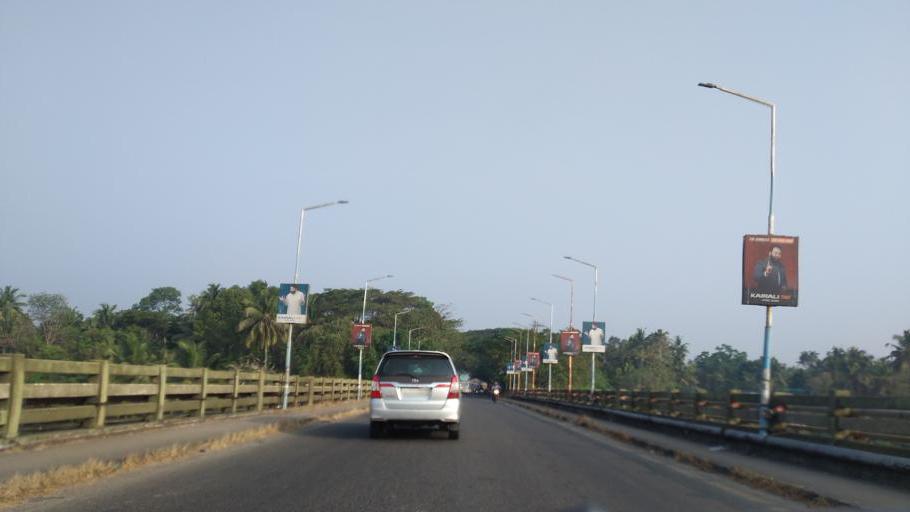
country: IN
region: Kerala
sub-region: Thrissur District
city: Kodungallur
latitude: 10.1998
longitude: 76.2006
